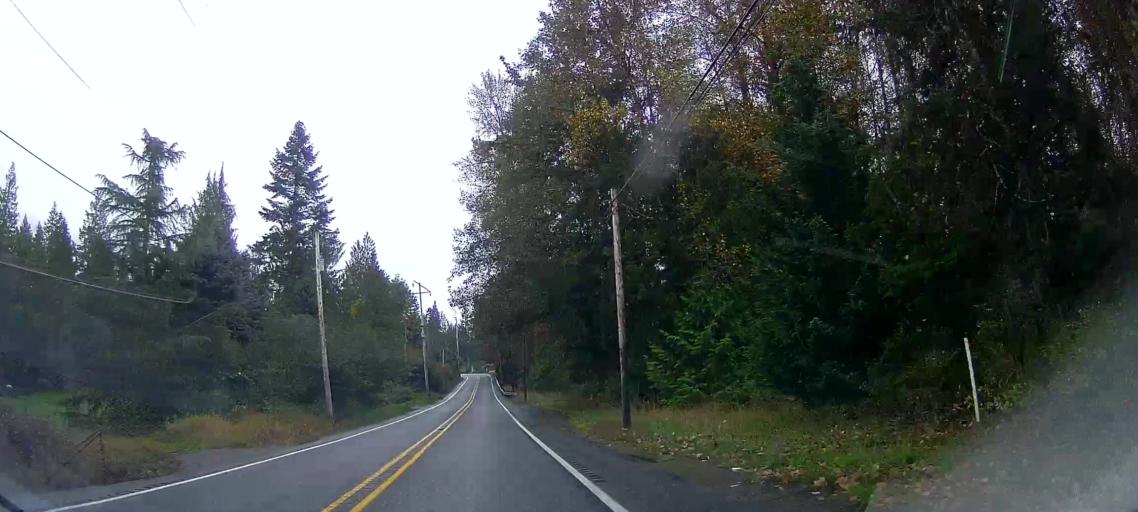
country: US
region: Washington
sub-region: Snohomish County
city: Darrington
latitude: 48.5207
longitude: -121.7102
